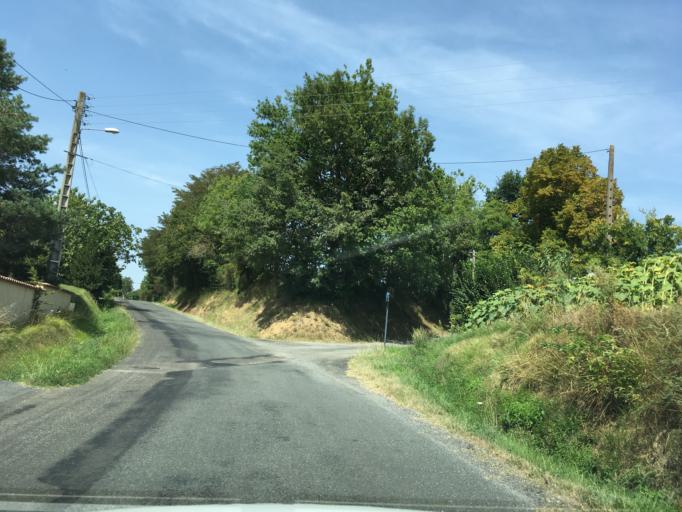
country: FR
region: Midi-Pyrenees
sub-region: Departement du Tarn
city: Roquecourbe
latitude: 43.6575
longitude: 2.2388
